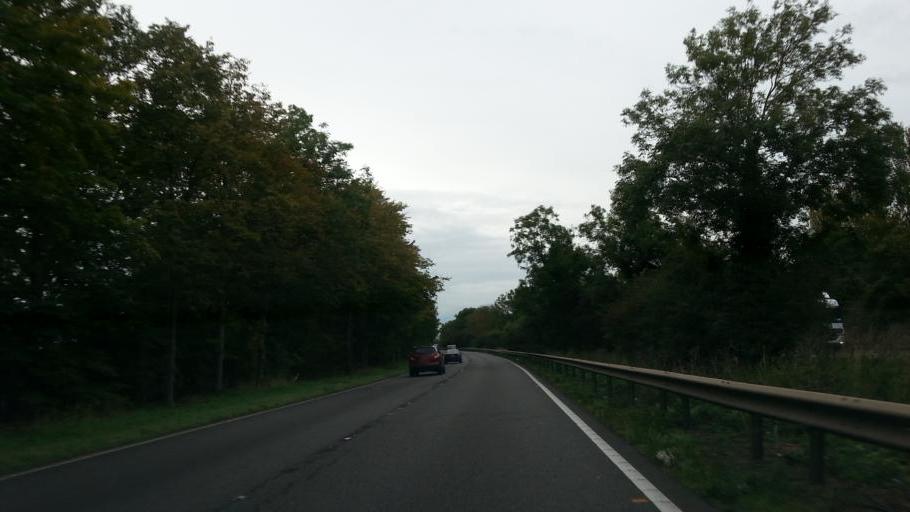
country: GB
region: England
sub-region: Peterborough
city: Castor
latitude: 52.5393
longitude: -0.3251
